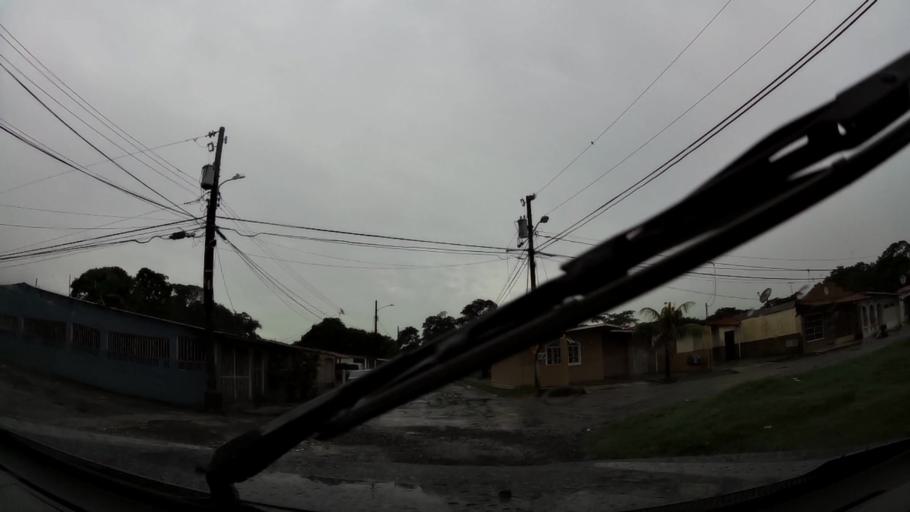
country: PA
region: Colon
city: Puerto Pilon
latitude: 9.3618
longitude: -79.8037
